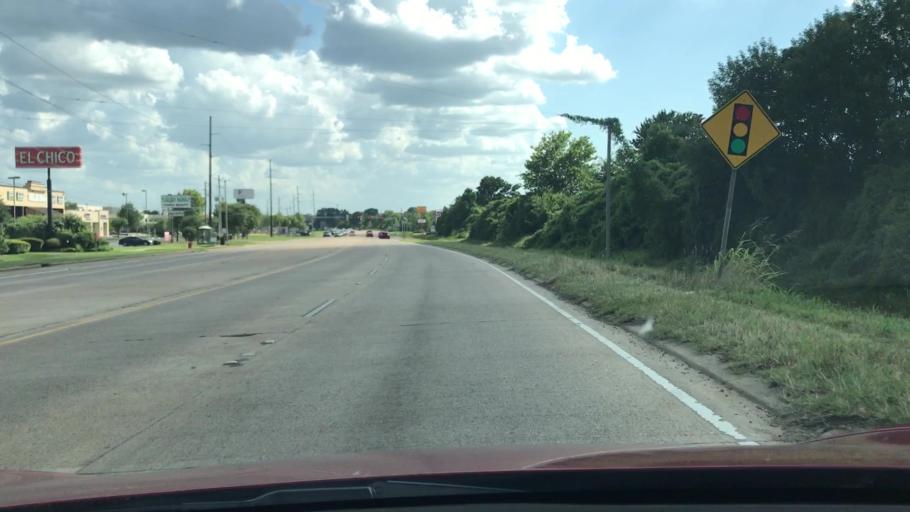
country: US
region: Louisiana
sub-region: Bossier Parish
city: Bossier City
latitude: 32.4297
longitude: -93.7160
